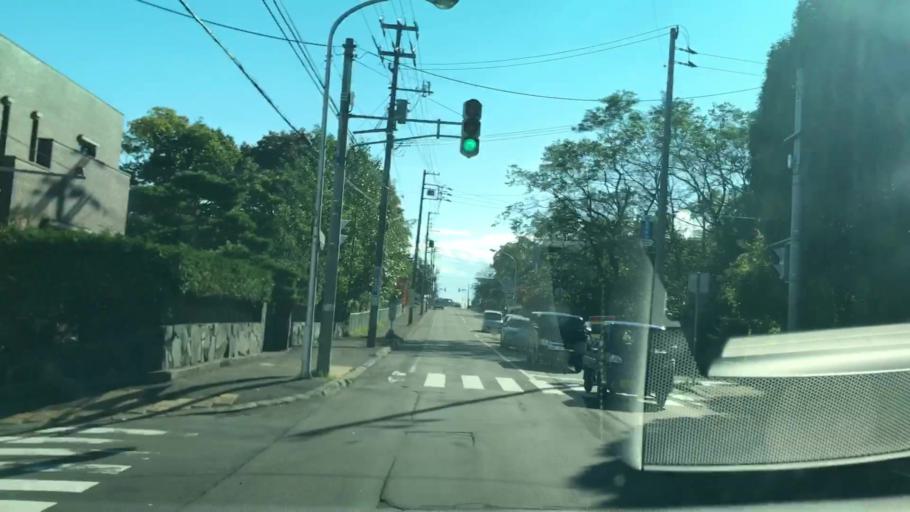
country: JP
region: Hokkaido
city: Sapporo
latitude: 43.0378
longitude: 141.3238
